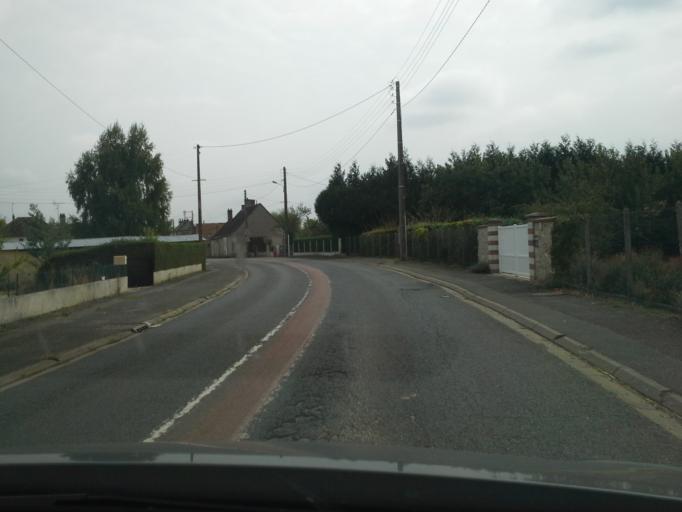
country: FR
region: Centre
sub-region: Departement du Loir-et-Cher
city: Vendome
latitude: 47.7309
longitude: 1.0850
